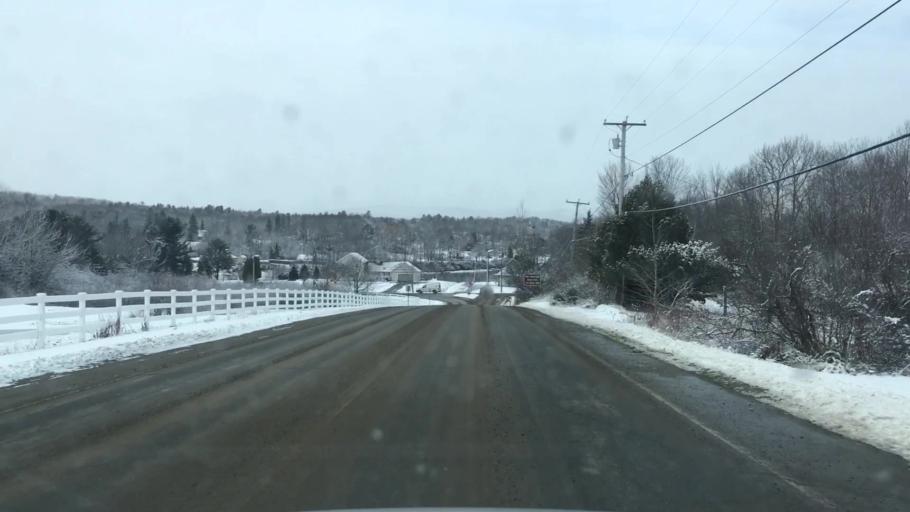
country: US
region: Maine
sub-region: Knox County
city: Rockland
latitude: 44.0752
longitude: -69.1010
